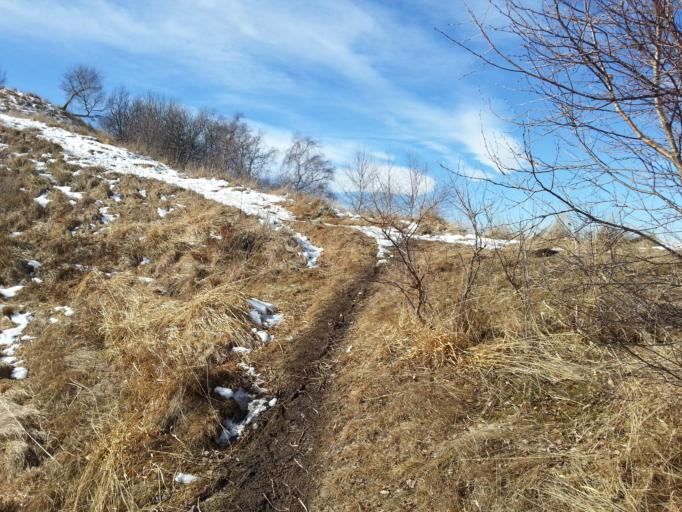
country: IT
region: Lombardy
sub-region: Provincia di Como
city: Lemna
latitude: 45.8344
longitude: 9.1433
